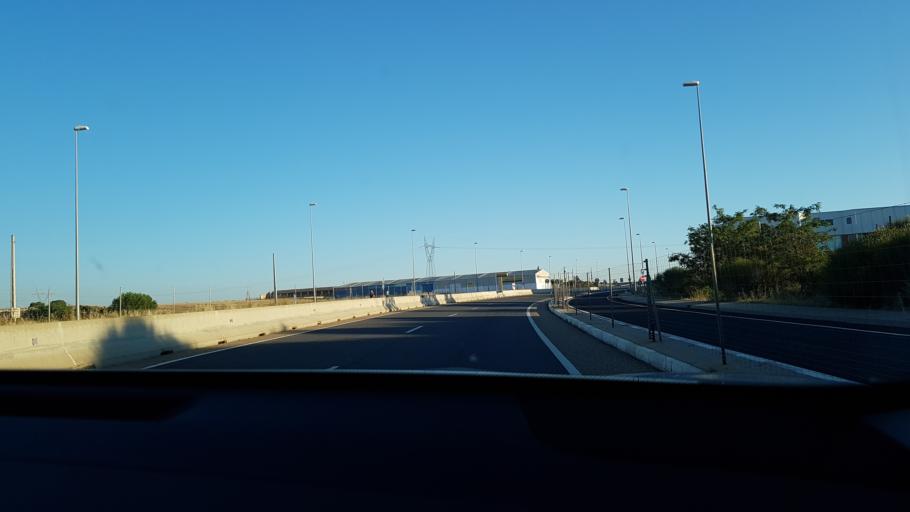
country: ES
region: Castille and Leon
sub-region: Provincia de Zamora
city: Roales
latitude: 41.5369
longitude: -5.7634
